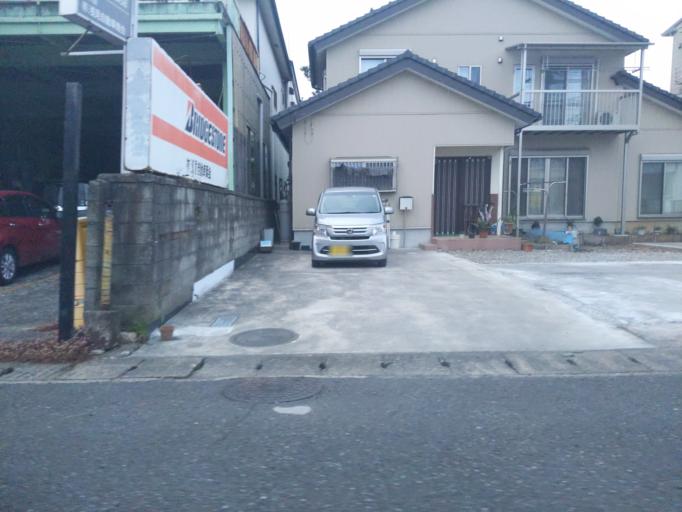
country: JP
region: Saitama
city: Koshigaya
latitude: 35.8641
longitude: 139.7951
